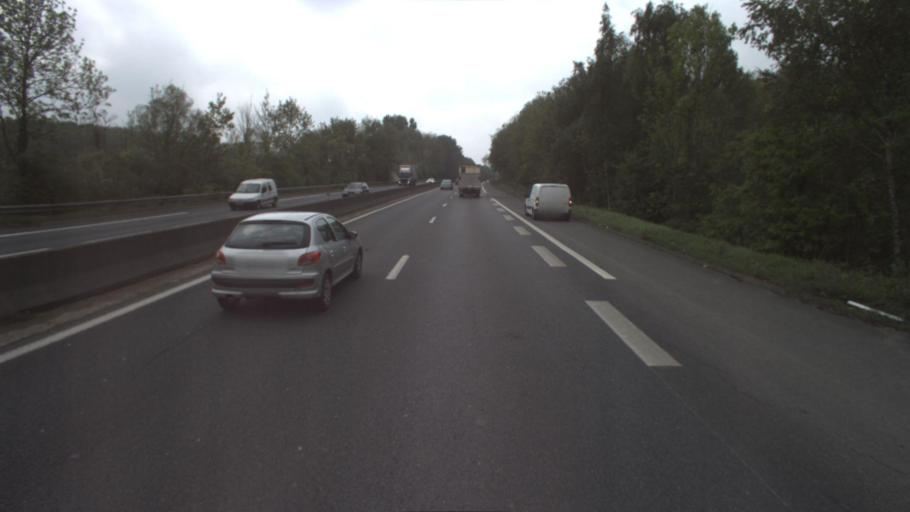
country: FR
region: Ile-de-France
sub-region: Departement de Seine-et-Marne
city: Saint-Mard
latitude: 49.0531
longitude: 2.6985
